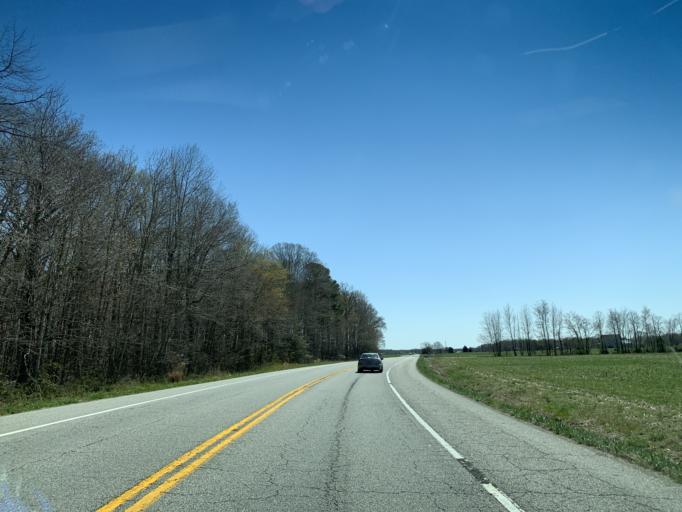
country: US
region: Maryland
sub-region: Queen Anne's County
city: Centreville
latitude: 38.9910
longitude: -76.0305
